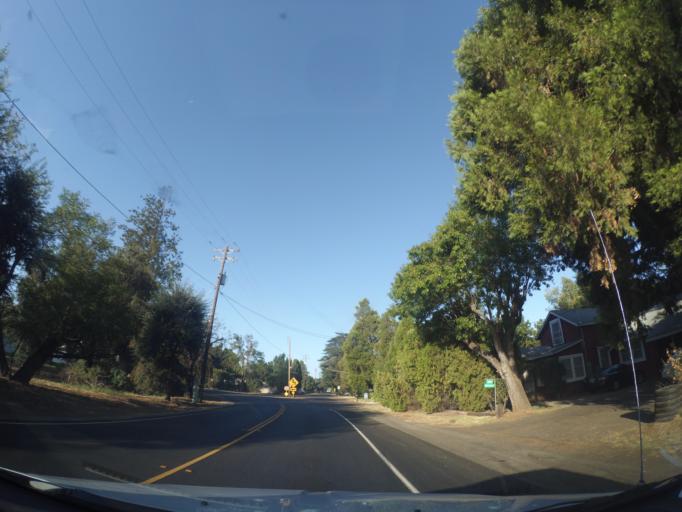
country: US
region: California
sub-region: Merced County
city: Winton
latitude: 37.5213
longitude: -120.4367
